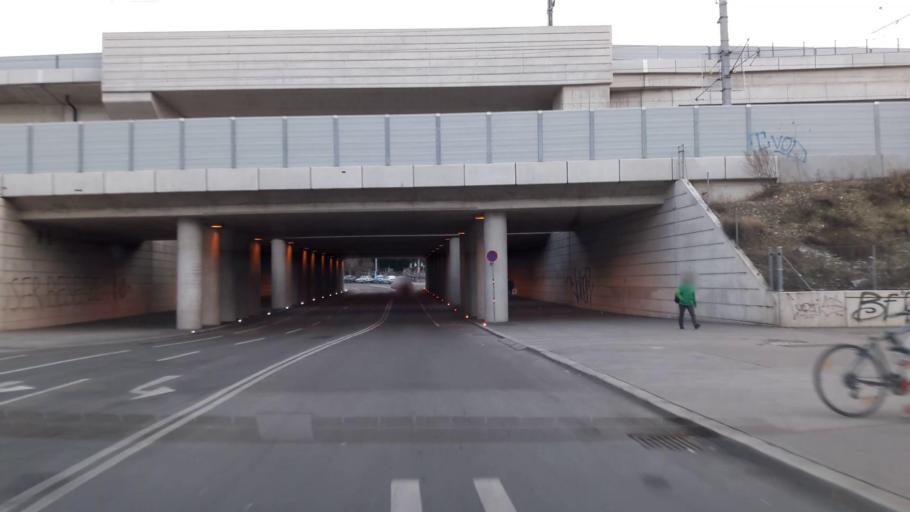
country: AT
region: Vienna
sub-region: Wien Stadt
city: Vienna
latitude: 48.1826
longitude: 16.3646
